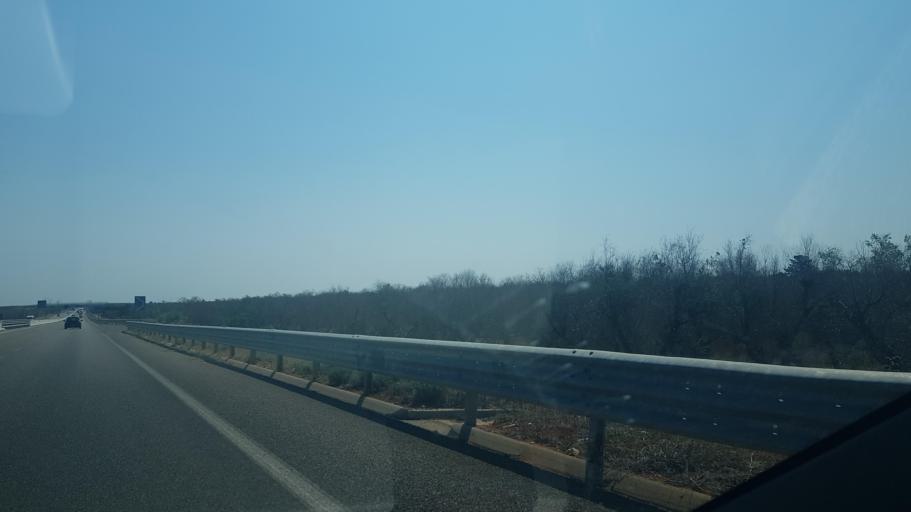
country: IT
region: Apulia
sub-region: Provincia di Lecce
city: Giurdignano
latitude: 40.1352
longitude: 18.4066
